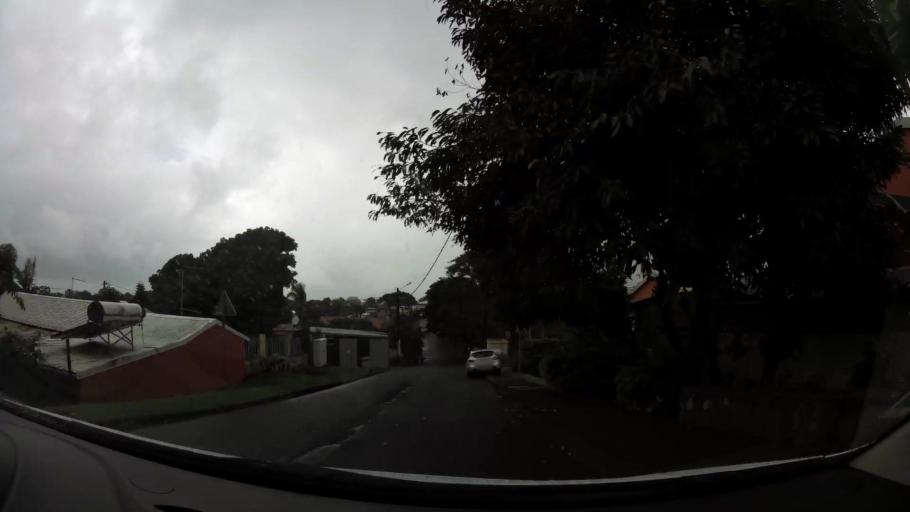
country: RE
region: Reunion
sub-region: Reunion
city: Saint-Andre
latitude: -20.9598
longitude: 55.6469
